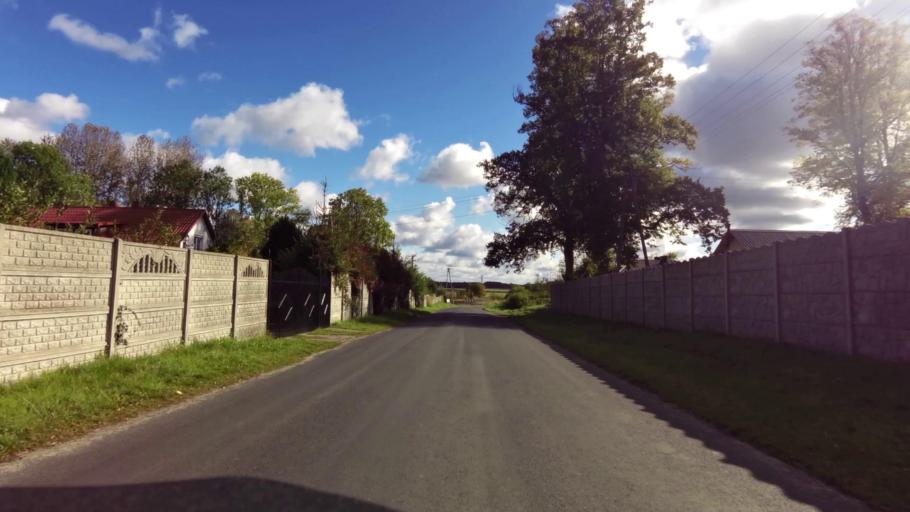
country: PL
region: West Pomeranian Voivodeship
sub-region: Powiat bialogardzki
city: Bialogard
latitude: 53.9987
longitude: 16.0604
